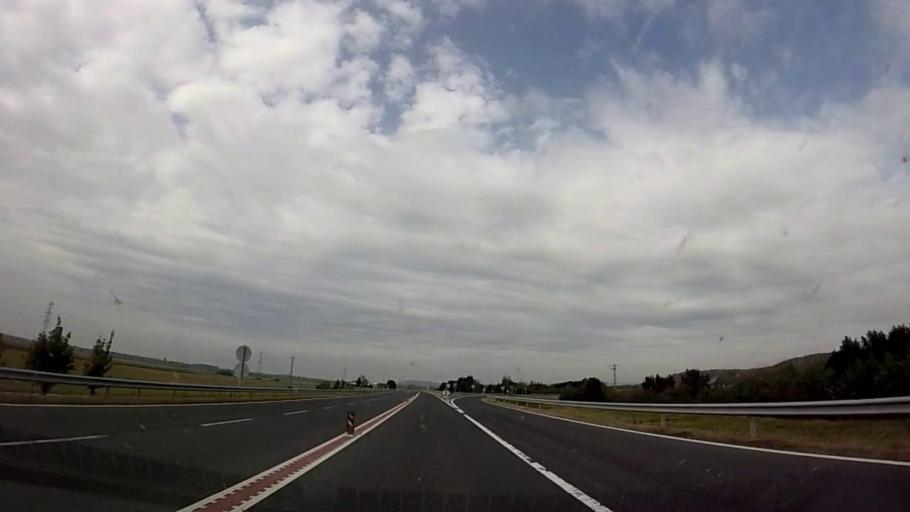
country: HR
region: Medimurska
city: Domasinec
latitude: 46.5021
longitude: 16.6125
